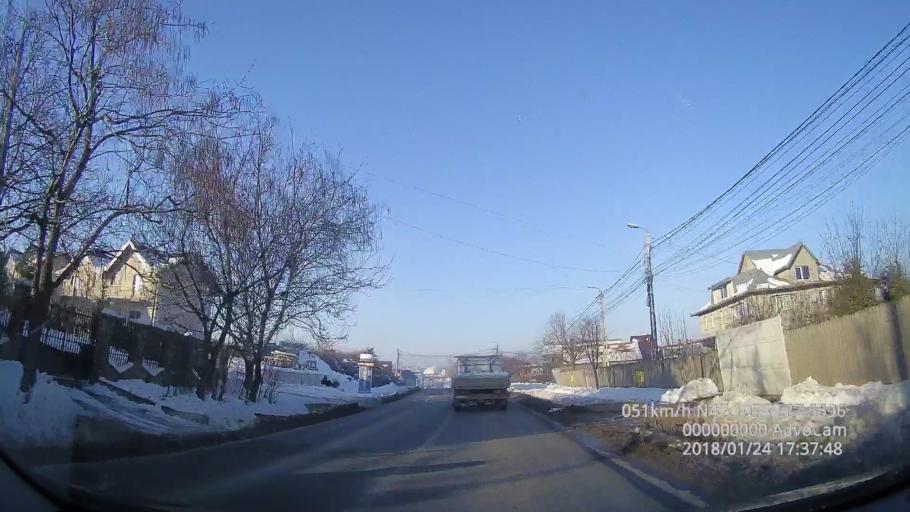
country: RO
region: Iasi
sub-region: Comuna Ciurea
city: Lunca Cetatuii
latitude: 47.1079
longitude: 27.5596
